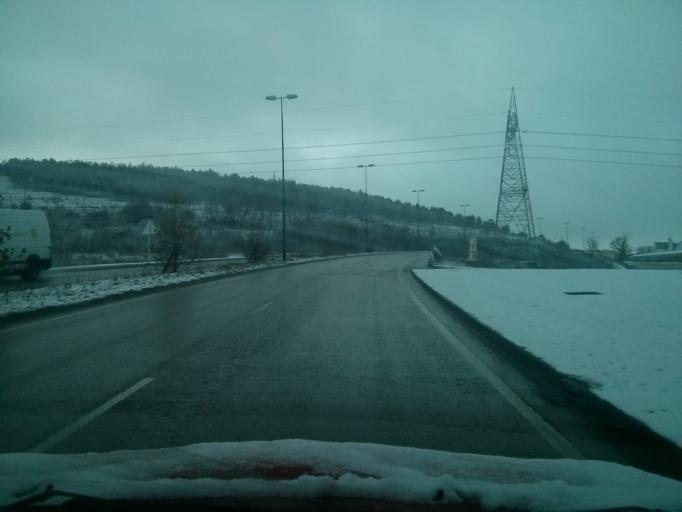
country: ES
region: Castille and Leon
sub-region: Provincia de Burgos
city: Burgos
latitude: 42.3650
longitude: -3.6945
